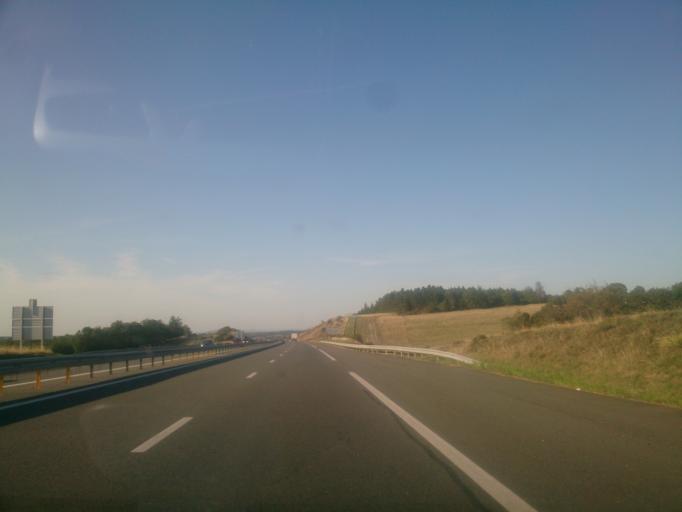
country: FR
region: Midi-Pyrenees
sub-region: Departement du Lot
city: Le Vigan
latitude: 44.6666
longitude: 1.5697
